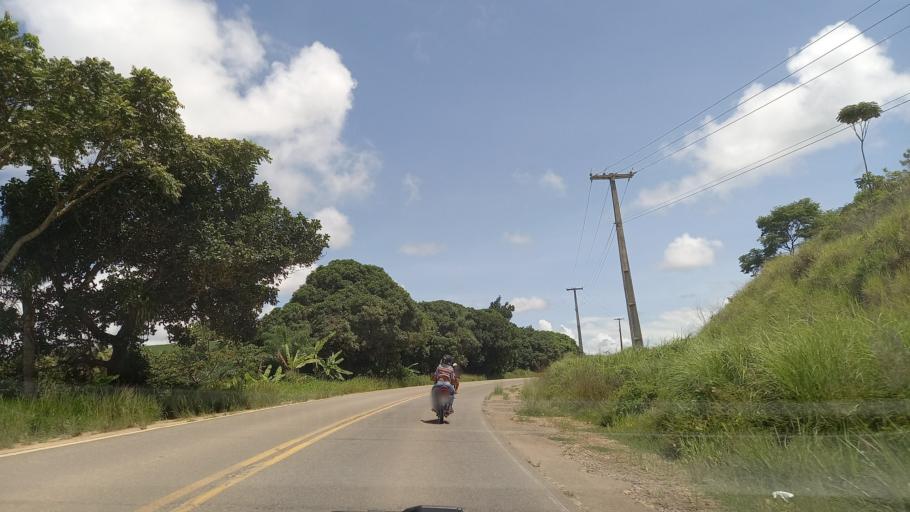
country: BR
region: Pernambuco
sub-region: Sirinhaem
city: Sirinhaem
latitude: -8.6179
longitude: -35.1215
